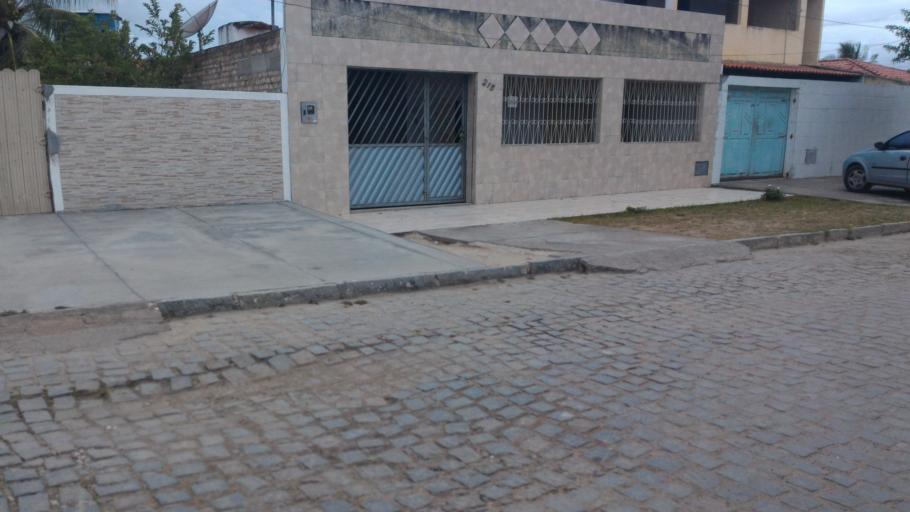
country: BR
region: Bahia
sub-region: Serrinha
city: Serrinha
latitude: -11.7480
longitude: -39.1906
